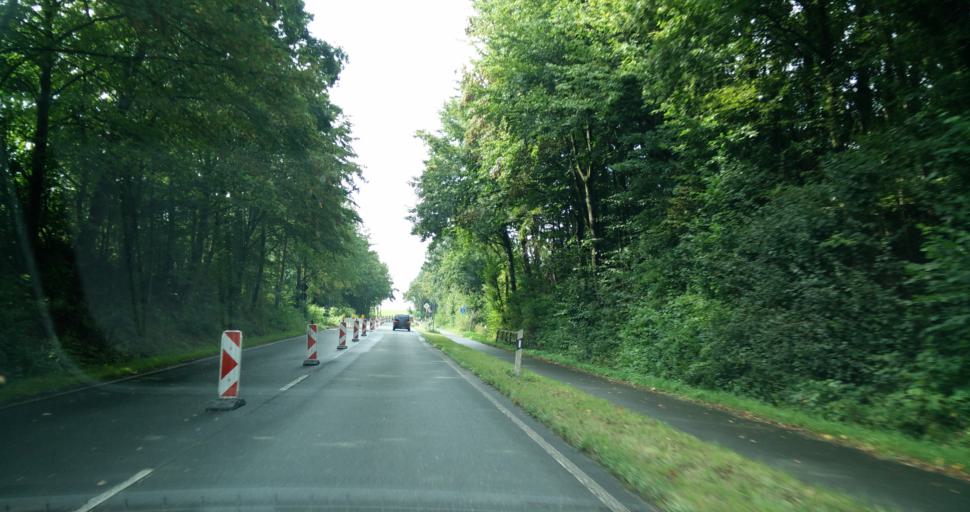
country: DE
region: North Rhine-Westphalia
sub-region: Regierungsbezirk Dusseldorf
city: Mettmann
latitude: 51.2412
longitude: 6.9537
